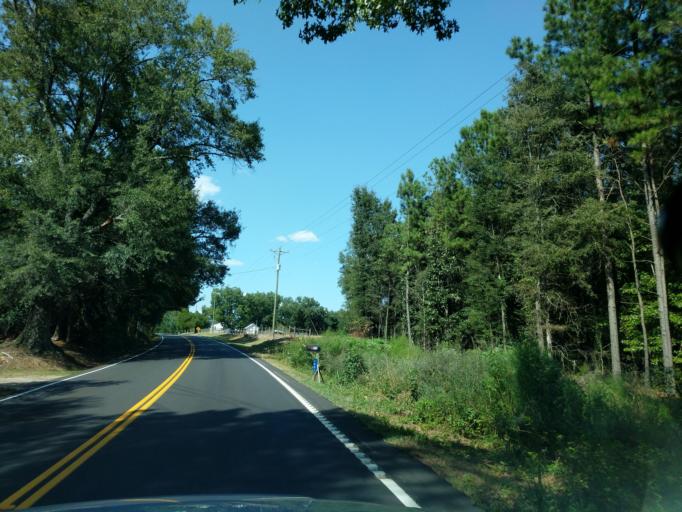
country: US
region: South Carolina
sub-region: Lexington County
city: Leesville
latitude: 33.9582
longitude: -81.5307
